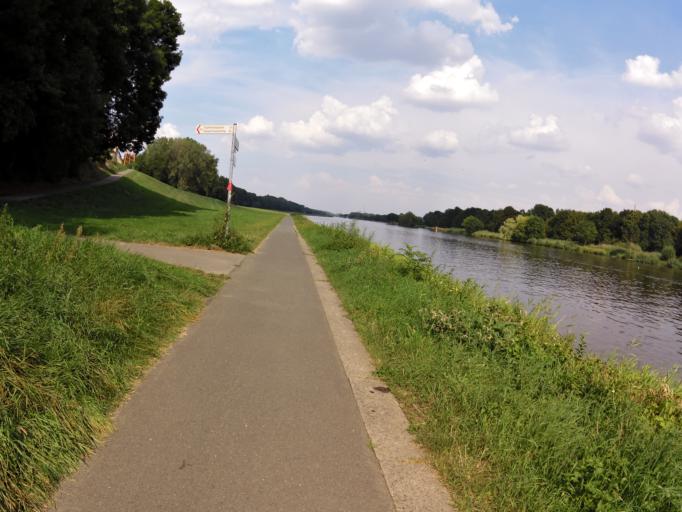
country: DE
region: North Rhine-Westphalia
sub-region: Regierungsbezirk Detmold
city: Minden
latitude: 52.3258
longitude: 8.9263
